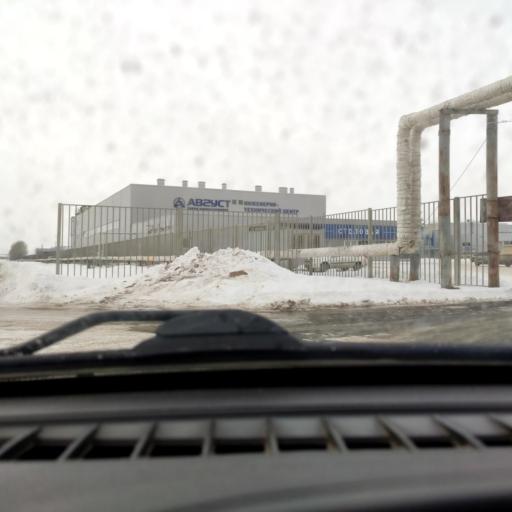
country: RU
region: Samara
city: Podstepki
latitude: 53.5867
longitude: 49.2109
